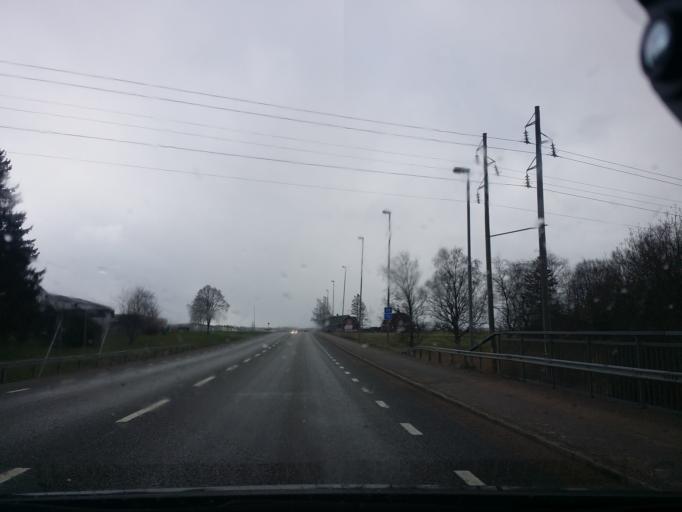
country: SE
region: Vaestmanland
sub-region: Sala Kommun
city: Sala
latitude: 59.9160
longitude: 16.6230
